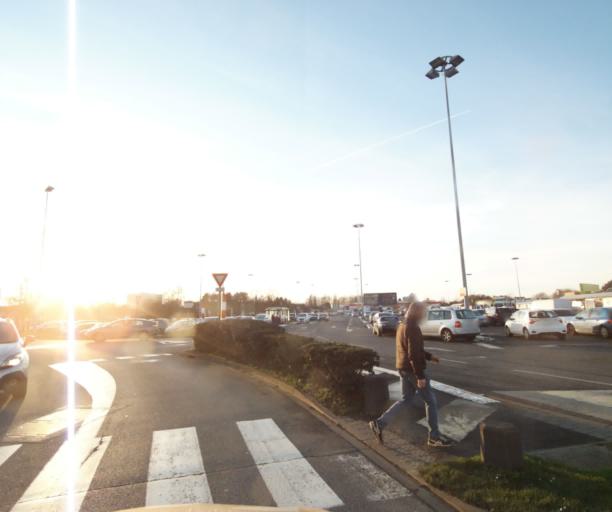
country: FR
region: Nord-Pas-de-Calais
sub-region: Departement du Nord
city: Aulnoy-lez-Valenciennes
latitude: 50.3347
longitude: 3.5189
